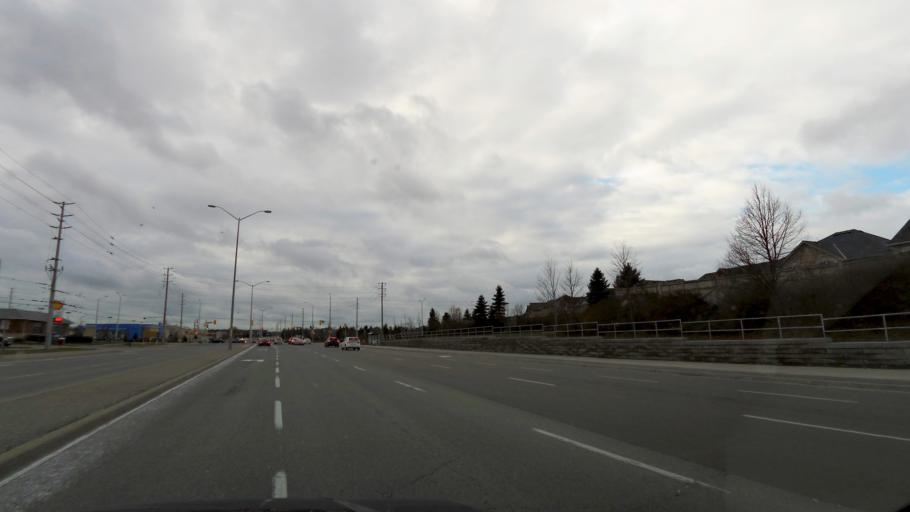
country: CA
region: Ontario
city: Brampton
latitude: 43.7645
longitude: -79.7211
